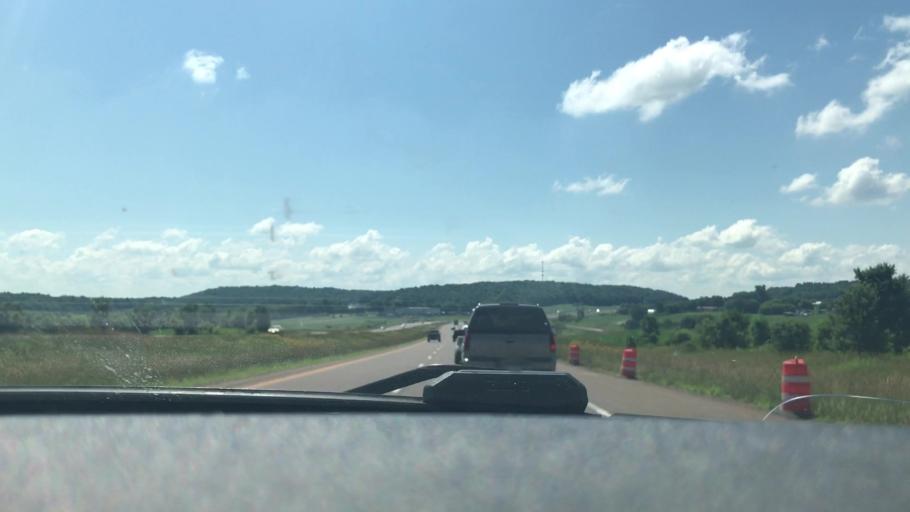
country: US
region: Wisconsin
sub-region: Chippewa County
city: Chippewa Falls
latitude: 44.9713
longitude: -91.4312
